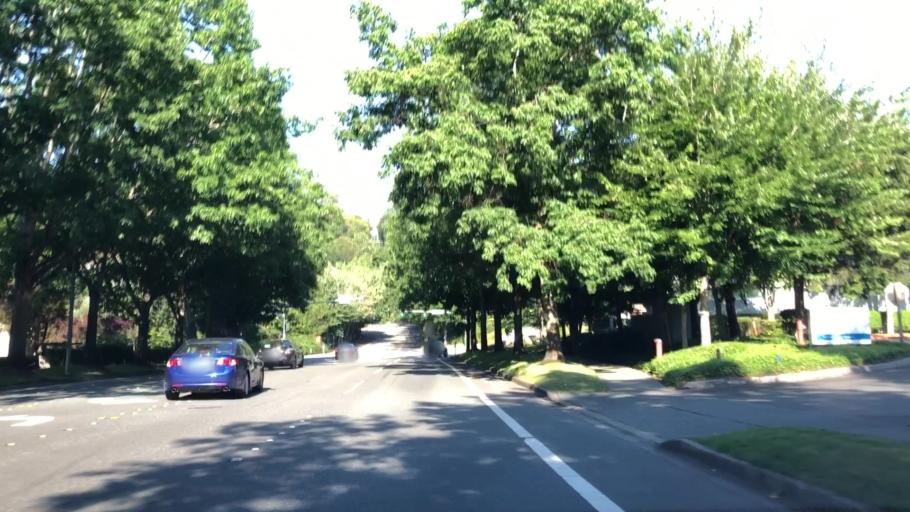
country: US
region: Washington
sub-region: King County
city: Woodinville
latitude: 47.7690
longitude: -122.1817
